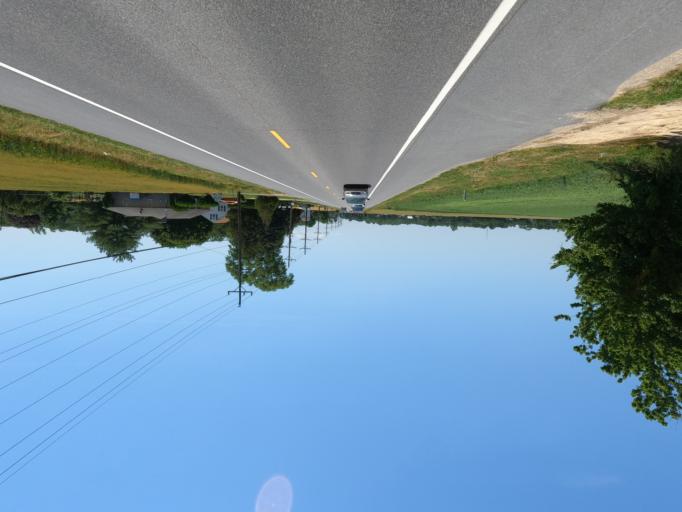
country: US
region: Delaware
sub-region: Sussex County
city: Milford
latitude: 38.9313
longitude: -75.4659
